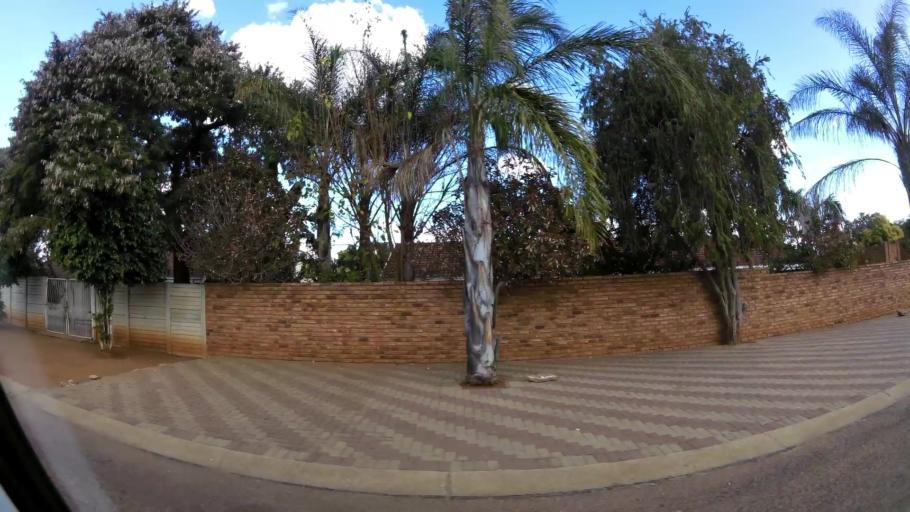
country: ZA
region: Limpopo
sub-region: Capricorn District Municipality
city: Polokwane
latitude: -23.9037
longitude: 29.4984
